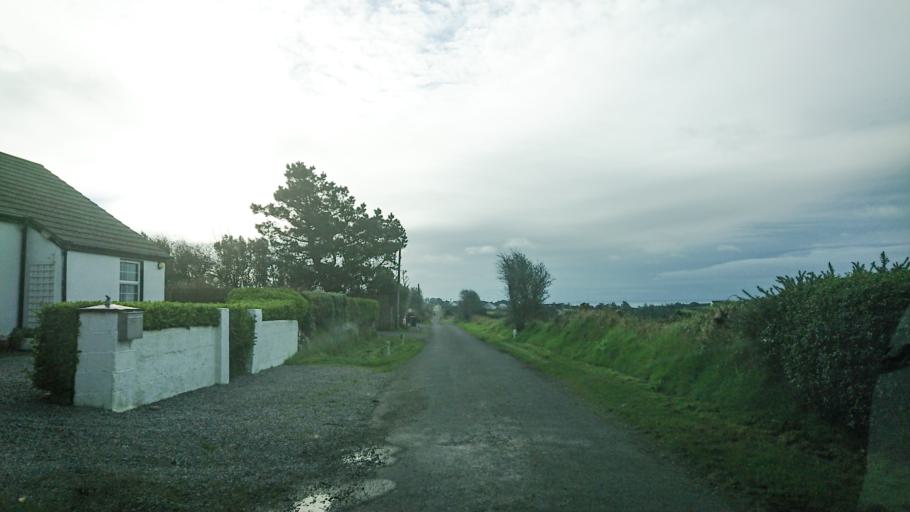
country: IE
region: Munster
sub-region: Waterford
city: Tra Mhor
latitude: 52.1476
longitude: -7.1930
